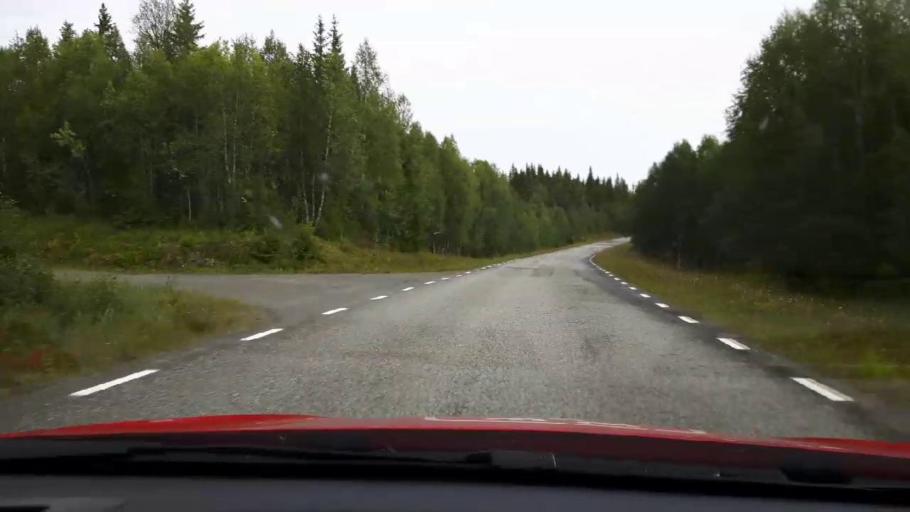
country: SE
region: Jaemtland
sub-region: Are Kommun
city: Are
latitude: 63.7393
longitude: 13.0379
